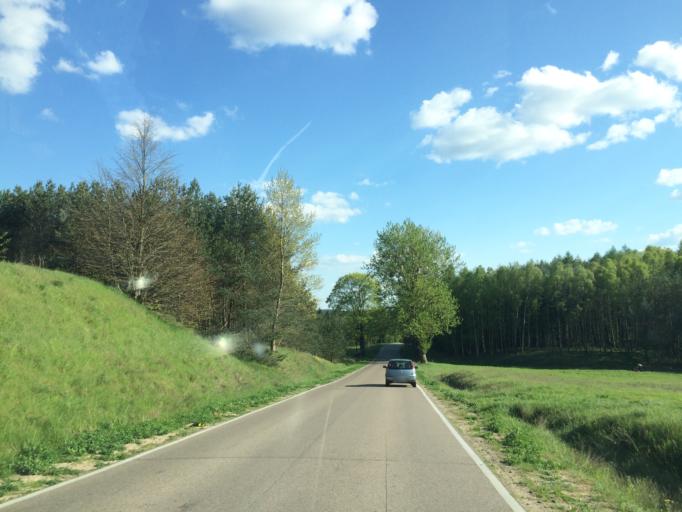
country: PL
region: Warmian-Masurian Voivodeship
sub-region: Powiat dzialdowski
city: Lidzbark
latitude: 53.3056
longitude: 19.8645
